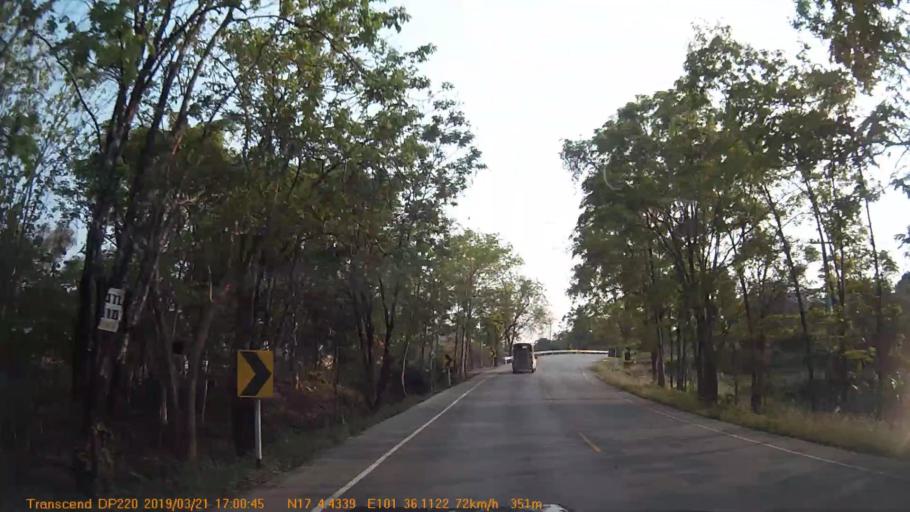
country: TH
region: Loei
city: Phu Luang
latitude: 17.0736
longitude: 101.6017
